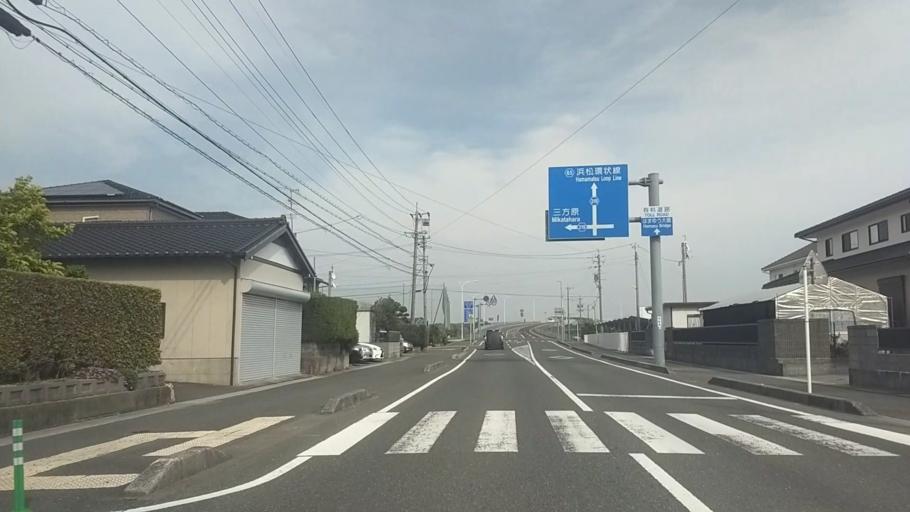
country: JP
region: Shizuoka
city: Kosai-shi
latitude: 34.7339
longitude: 137.6197
